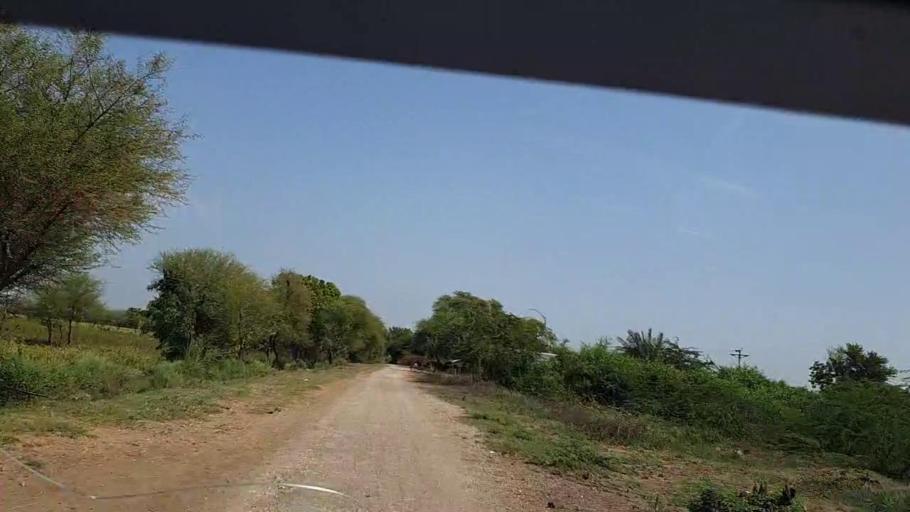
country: PK
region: Sindh
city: Rajo Khanani
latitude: 24.9256
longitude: 68.8749
